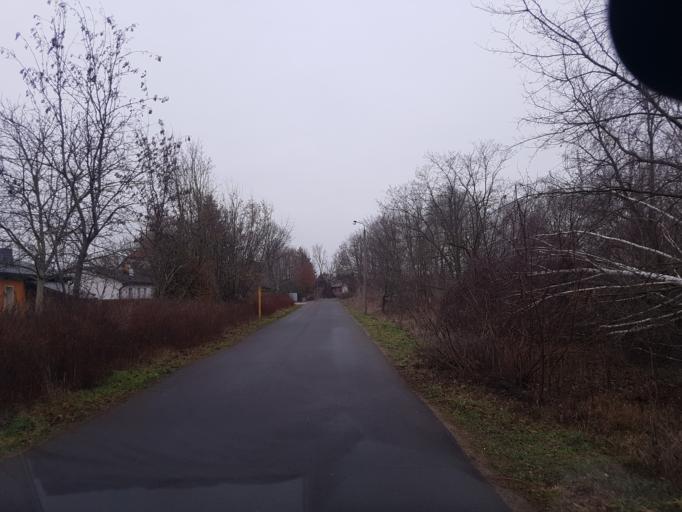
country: DE
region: Brandenburg
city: Falkenberg
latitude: 51.5915
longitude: 13.2625
